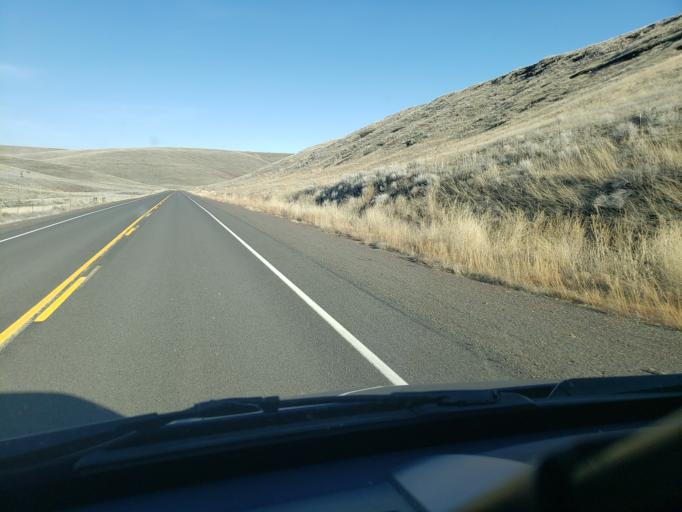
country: US
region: Oregon
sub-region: Umatilla County
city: Pilot Rock
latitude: 45.4660
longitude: -118.9215
